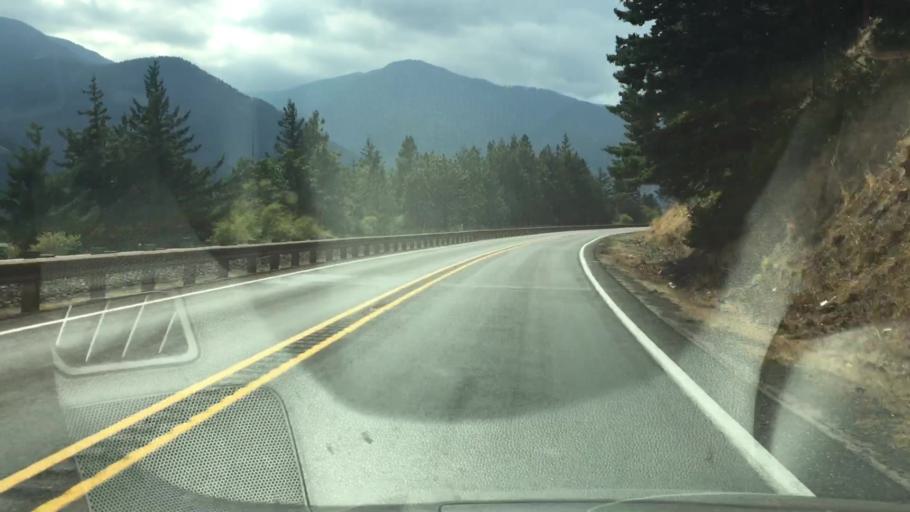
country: US
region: Washington
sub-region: Skamania County
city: Carson
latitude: 45.7056
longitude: -121.6844
